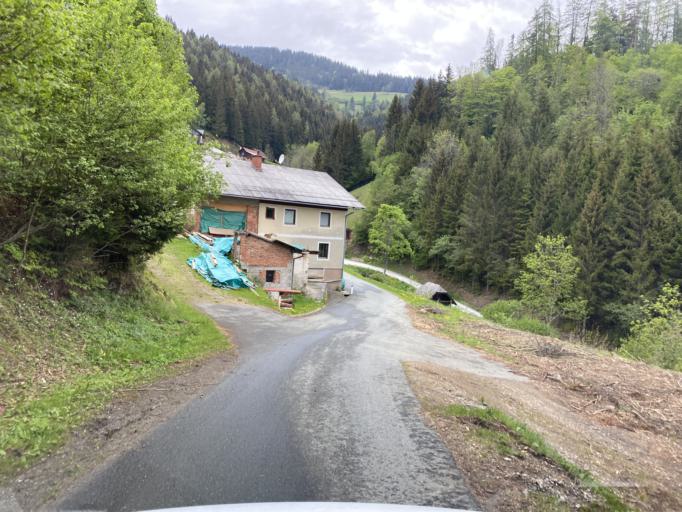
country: AT
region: Styria
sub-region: Politischer Bezirk Weiz
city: Koglhof
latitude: 47.3325
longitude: 15.6612
